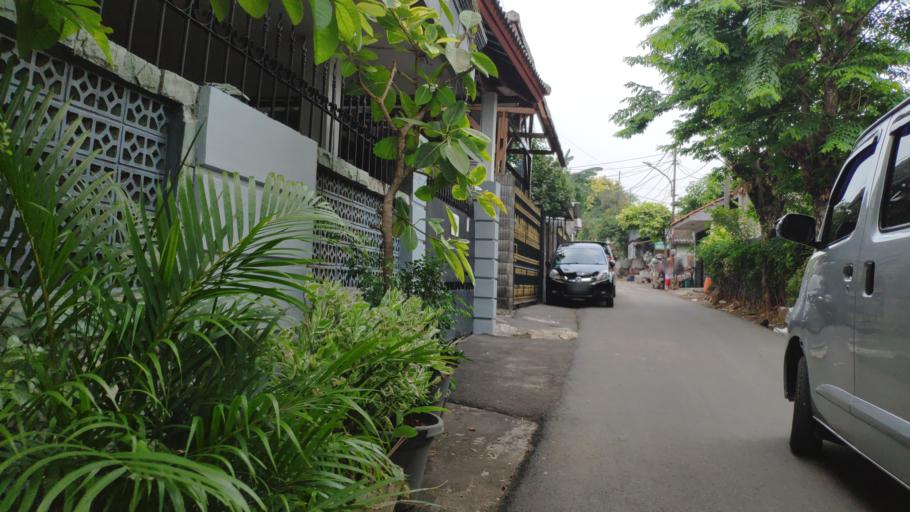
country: ID
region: Jakarta Raya
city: Jakarta
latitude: -6.2677
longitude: 106.7925
